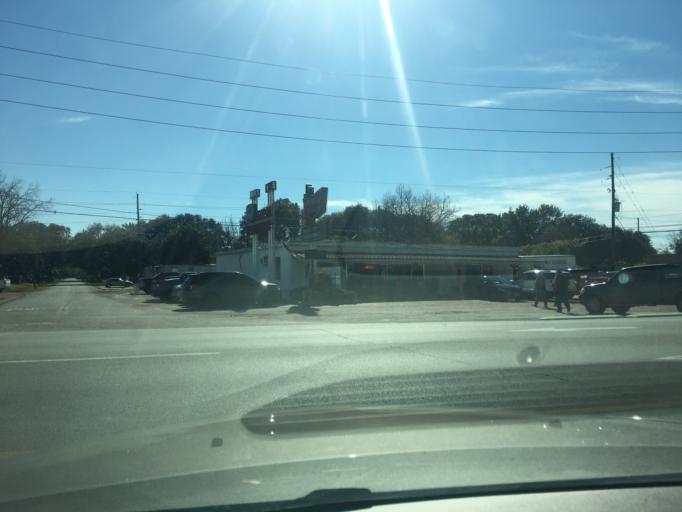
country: US
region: Texas
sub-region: Fort Bend County
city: Richmond
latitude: 29.5847
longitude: -95.7544
